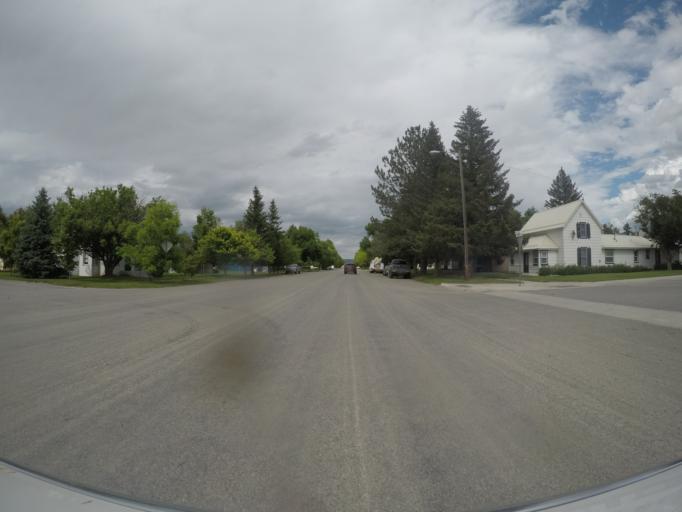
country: US
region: Montana
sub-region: Sweet Grass County
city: Big Timber
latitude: 45.8339
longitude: -109.9503
